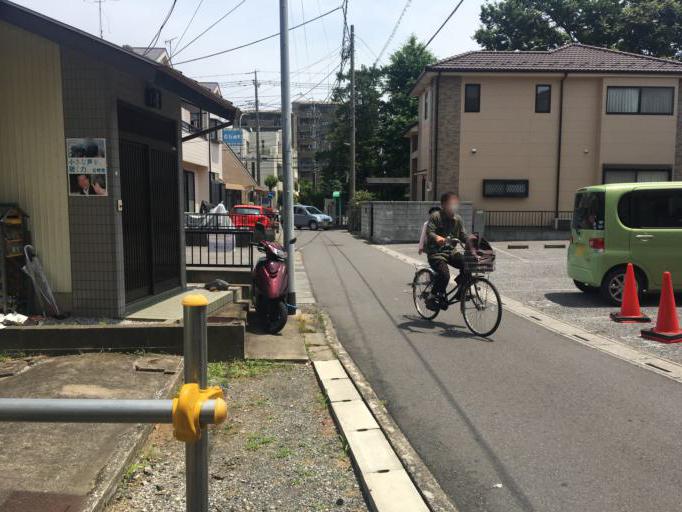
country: JP
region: Saitama
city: Koshigaya
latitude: 35.9021
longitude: 139.7813
